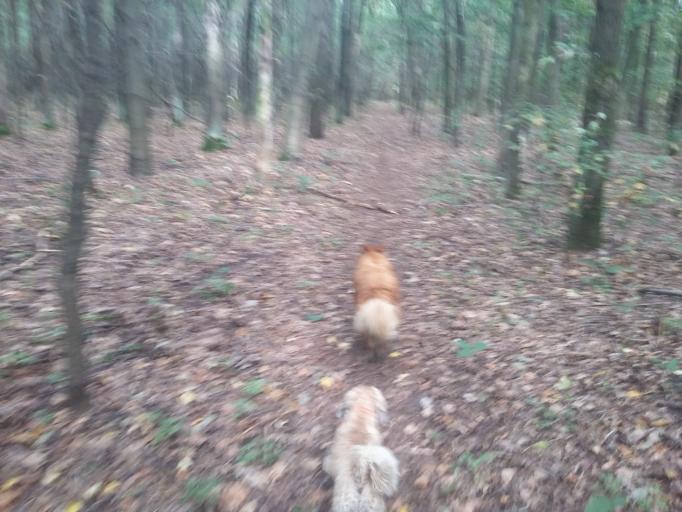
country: PL
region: Lodz Voivodeship
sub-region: Powiat pabianicki
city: Ksawerow
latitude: 51.7280
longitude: 19.3904
